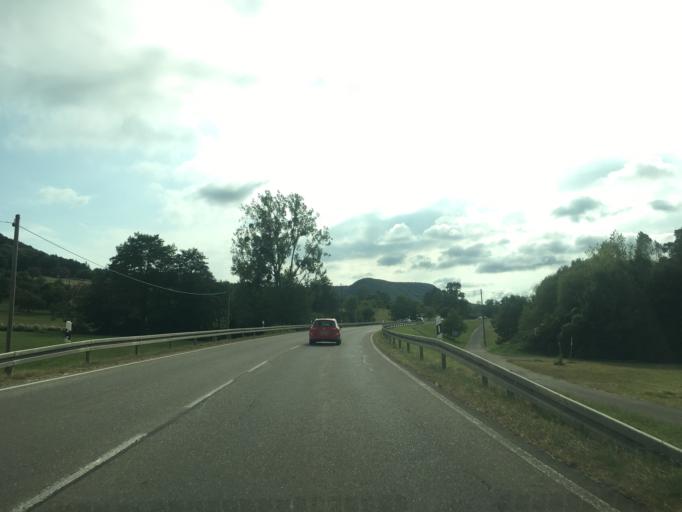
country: DE
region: Baden-Wuerttemberg
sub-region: Tuebingen Region
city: Gomaringen
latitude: 48.4460
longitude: 9.1537
